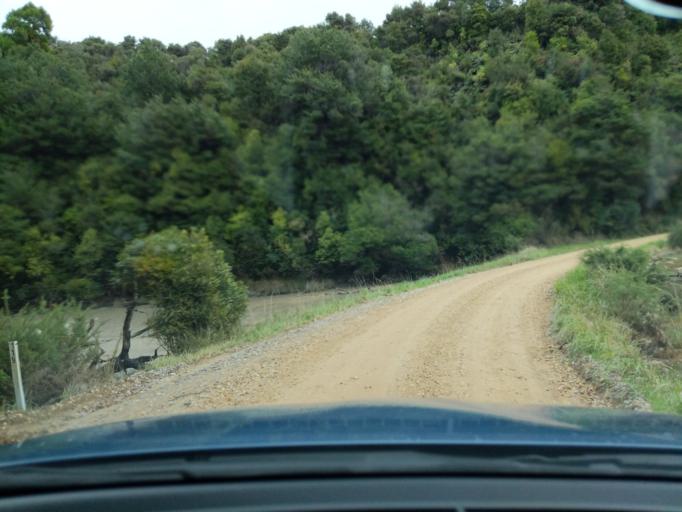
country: NZ
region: Tasman
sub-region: Tasman District
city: Takaka
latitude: -40.6264
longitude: 172.5181
